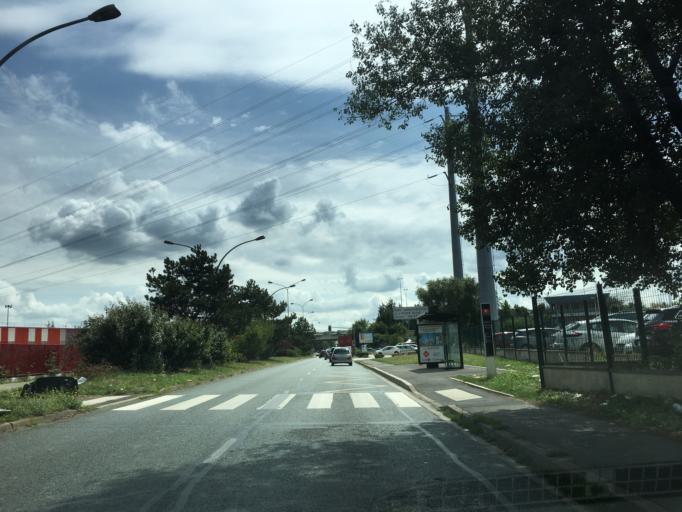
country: FR
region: Ile-de-France
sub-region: Departement du Val-de-Marne
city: Bonneuil-sur-Marne
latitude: 48.7599
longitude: 2.4799
